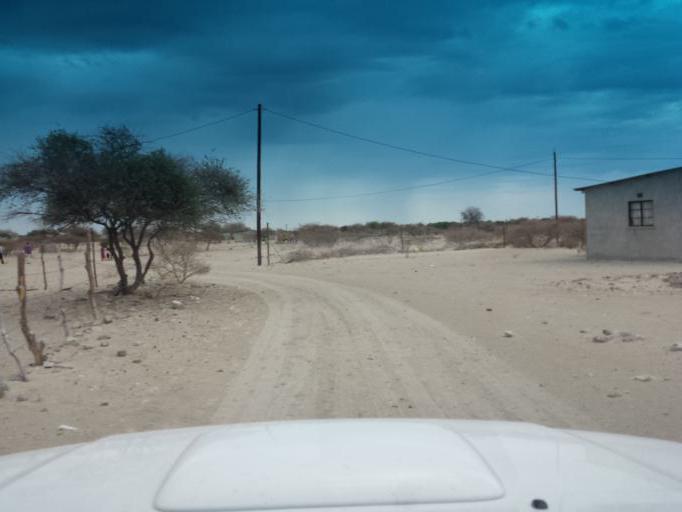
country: BW
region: Central
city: Mopipi
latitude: -21.1985
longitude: 24.8590
